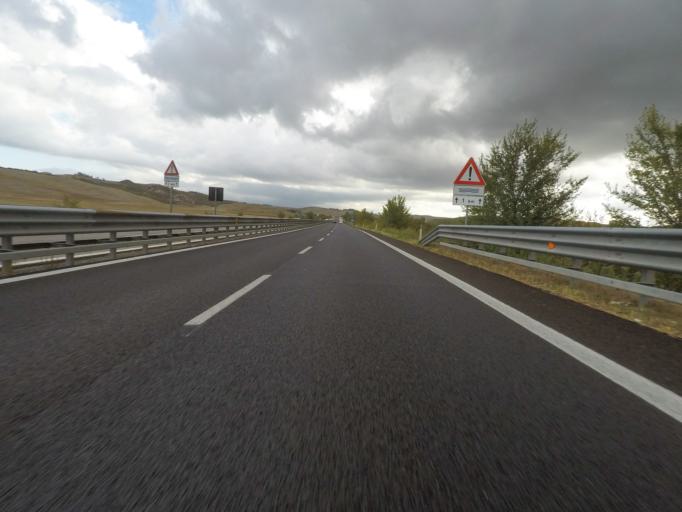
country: IT
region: Tuscany
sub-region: Provincia di Siena
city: Arbia
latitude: 43.3077
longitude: 11.4560
